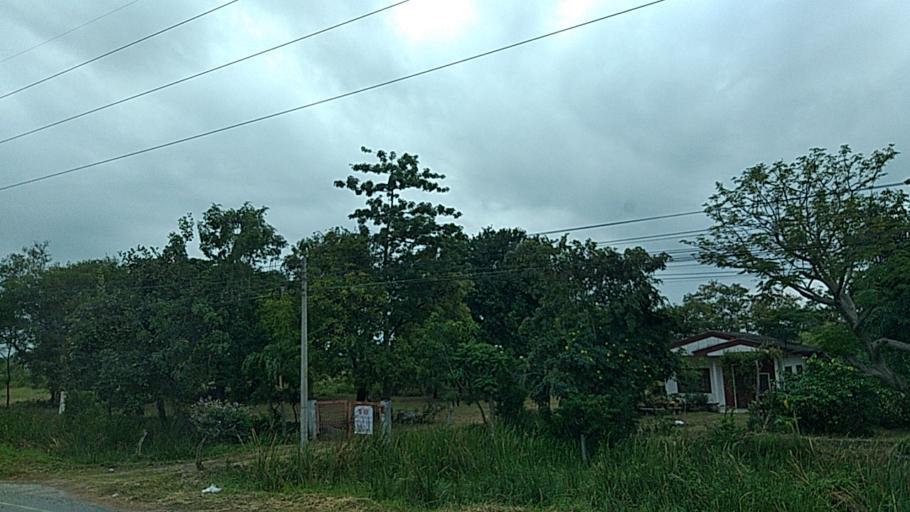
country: TH
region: Maha Sarakham
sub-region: Amphoe Borabue
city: Borabue
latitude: 16.0426
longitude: 103.1265
